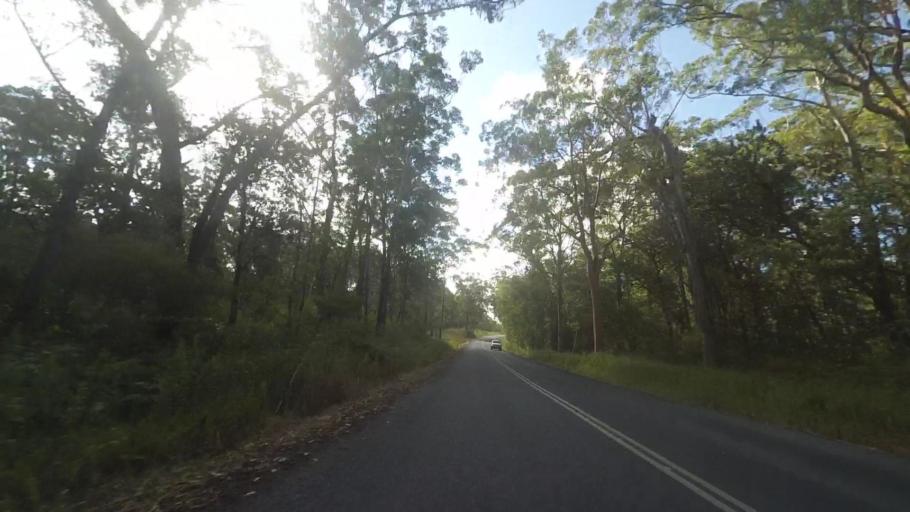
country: AU
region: New South Wales
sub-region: Great Lakes
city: Forster
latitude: -32.4243
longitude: 152.4985
